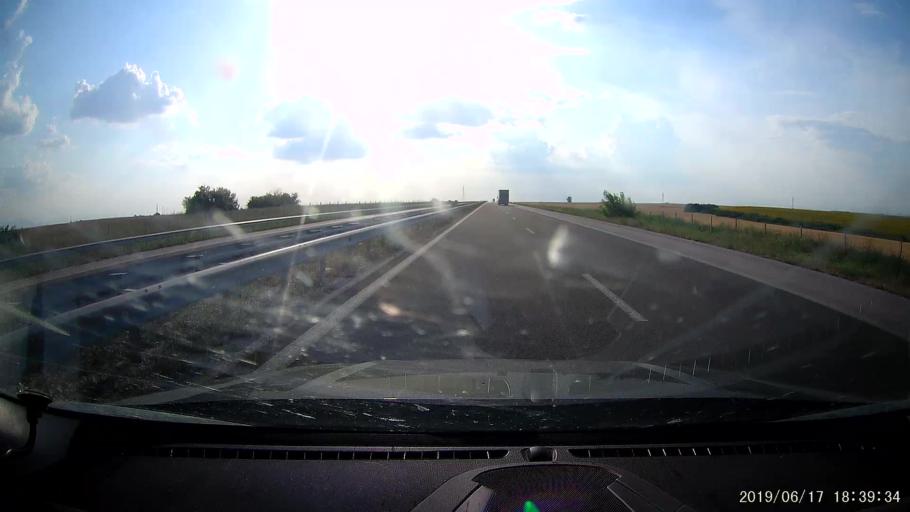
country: BG
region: Stara Zagora
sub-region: Obshtina Chirpan
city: Chirpan
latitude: 42.1463
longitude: 25.3036
